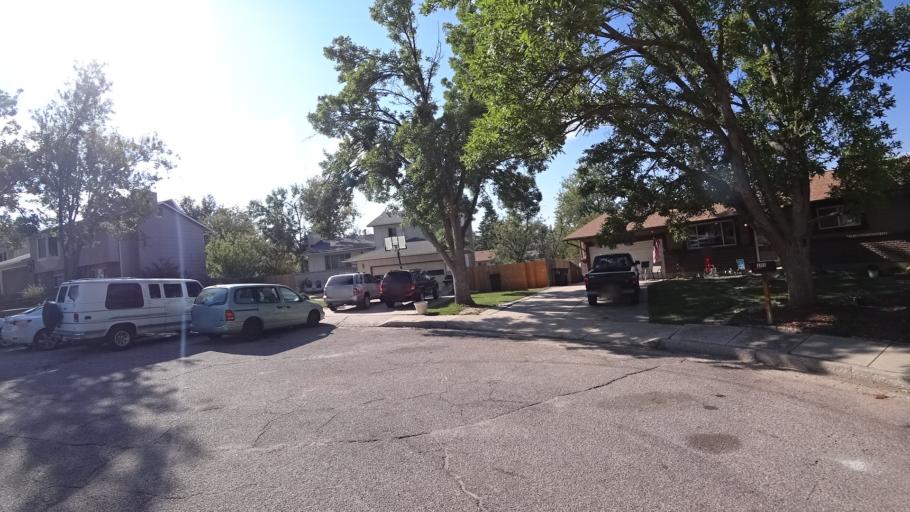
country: US
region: Colorado
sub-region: El Paso County
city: Cimarron Hills
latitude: 38.8821
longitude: -104.7330
